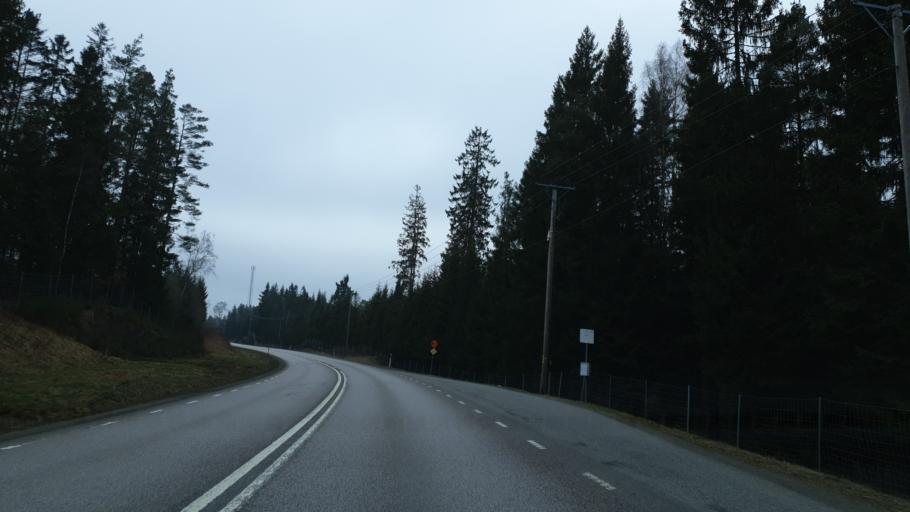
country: SE
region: Vaestra Goetaland
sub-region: Harryda Kommun
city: Hindas
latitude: 57.6464
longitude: 12.4054
